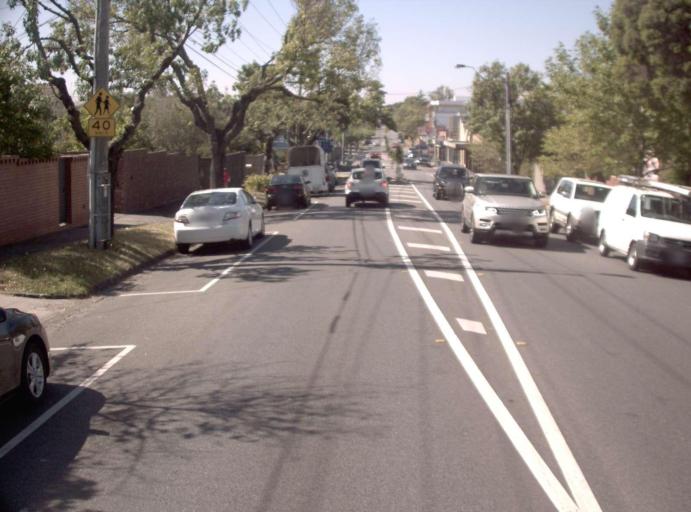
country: AU
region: Victoria
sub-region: Bayside
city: North Brighton
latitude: -37.9204
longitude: 145.0058
